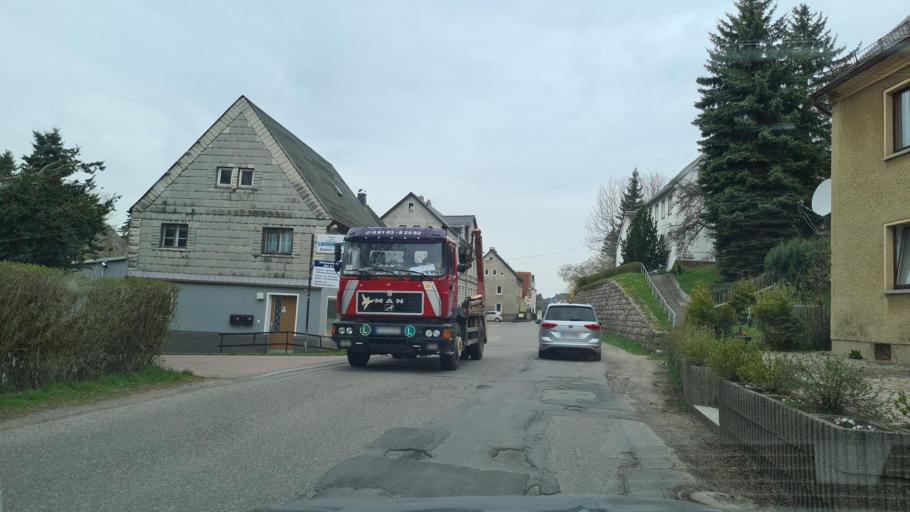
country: DE
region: Saxony
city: Claussnitz
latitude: 50.9004
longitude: 12.9162
